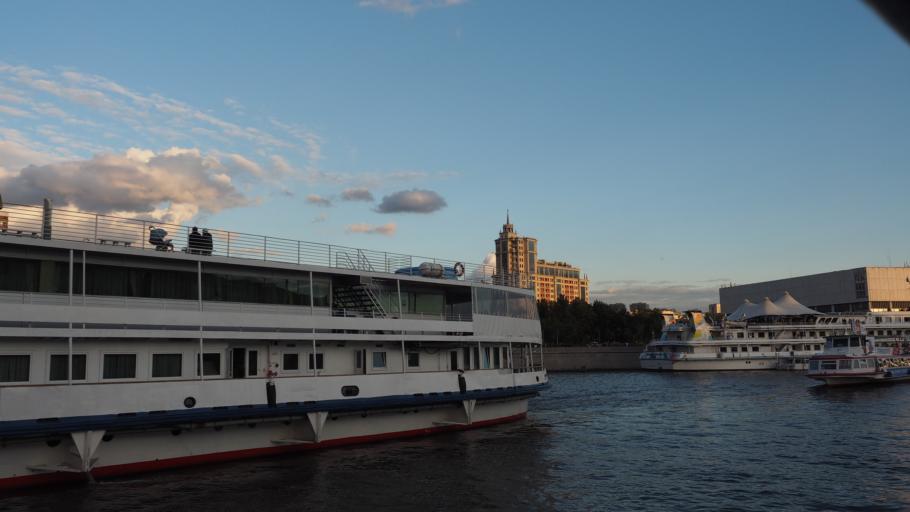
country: RU
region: Moscow
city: Moscow
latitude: 55.7390
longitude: 37.6067
